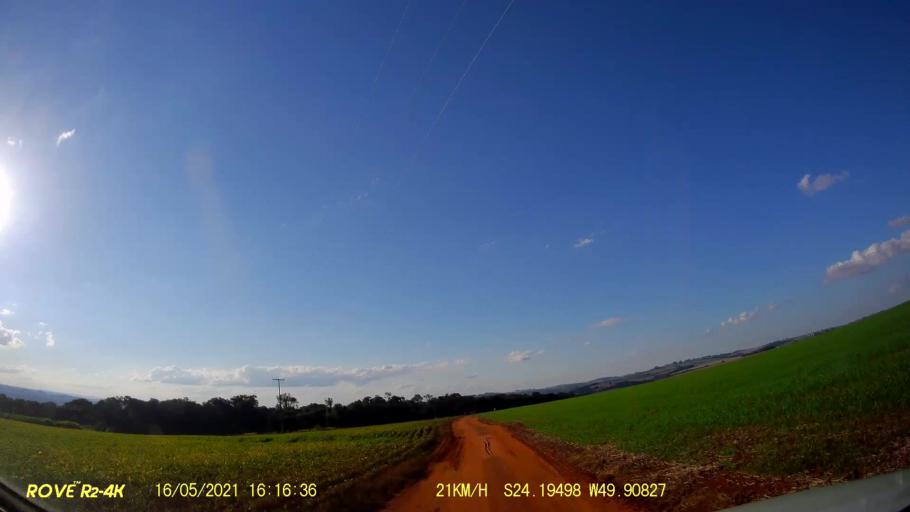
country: BR
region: Parana
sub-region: Jaguariaiva
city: Jaguariaiva
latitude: -24.1943
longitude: -49.9078
